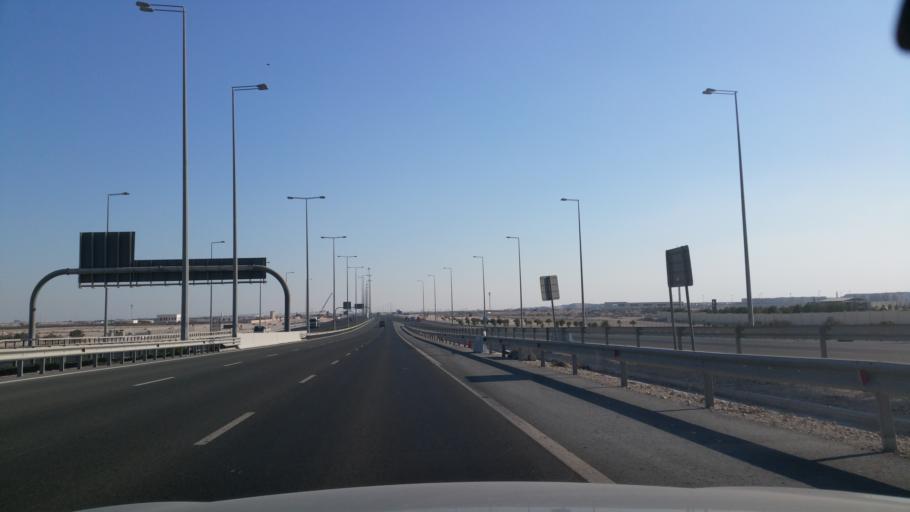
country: QA
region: Al Wakrah
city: Al Wukayr
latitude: 25.1617
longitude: 51.4725
